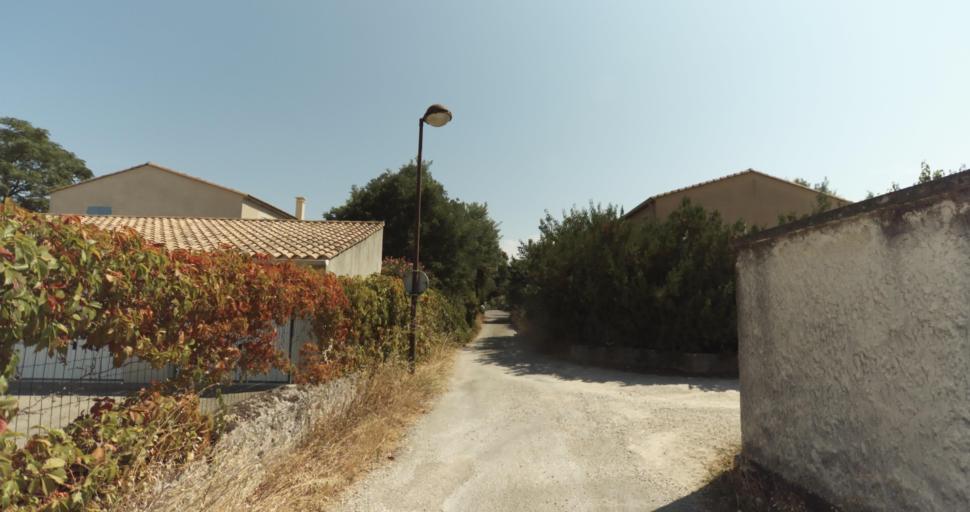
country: FR
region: Provence-Alpes-Cote d'Azur
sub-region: Departement du Vaucluse
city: Monteux
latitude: 44.0326
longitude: 4.9993
